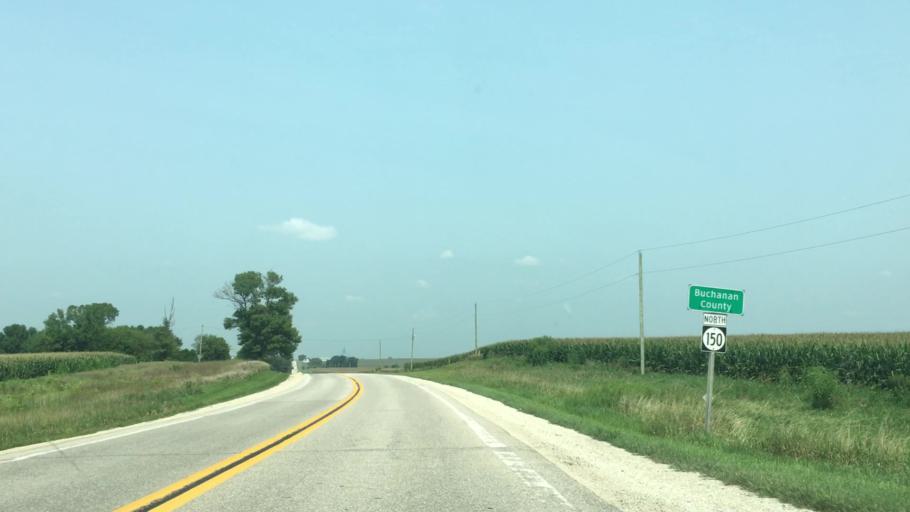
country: US
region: Iowa
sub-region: Benton County
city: Urbana
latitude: 42.2985
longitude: -91.8895
